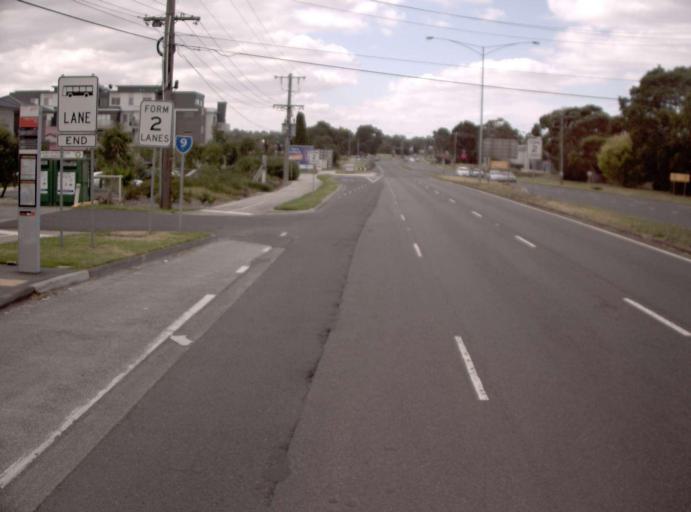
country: AU
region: Victoria
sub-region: Knox
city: Wantirna South
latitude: -37.8764
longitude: 145.2328
